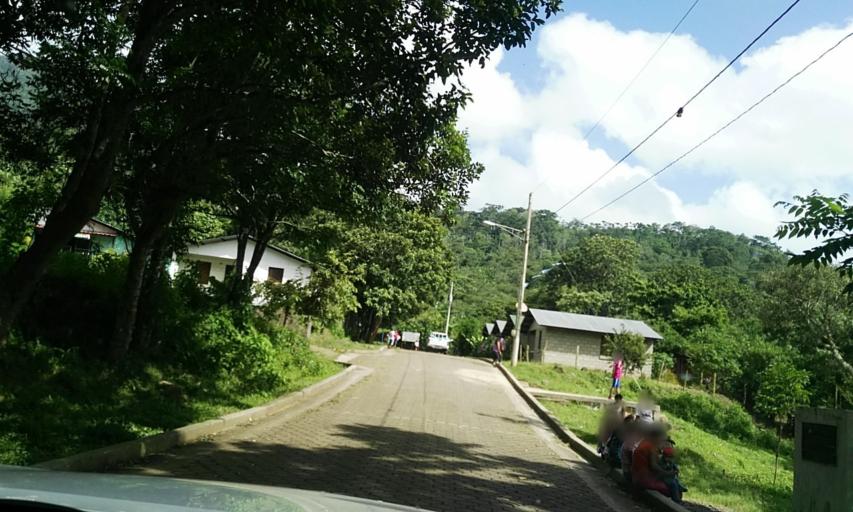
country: NI
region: Matagalpa
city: San Ramon
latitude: 12.9975
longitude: -85.8698
